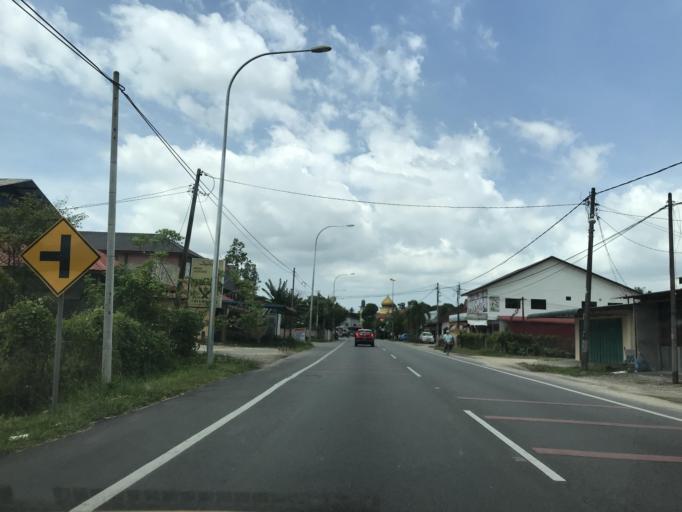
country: MY
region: Kelantan
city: Pasir Mas
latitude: 6.0515
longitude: 102.1862
